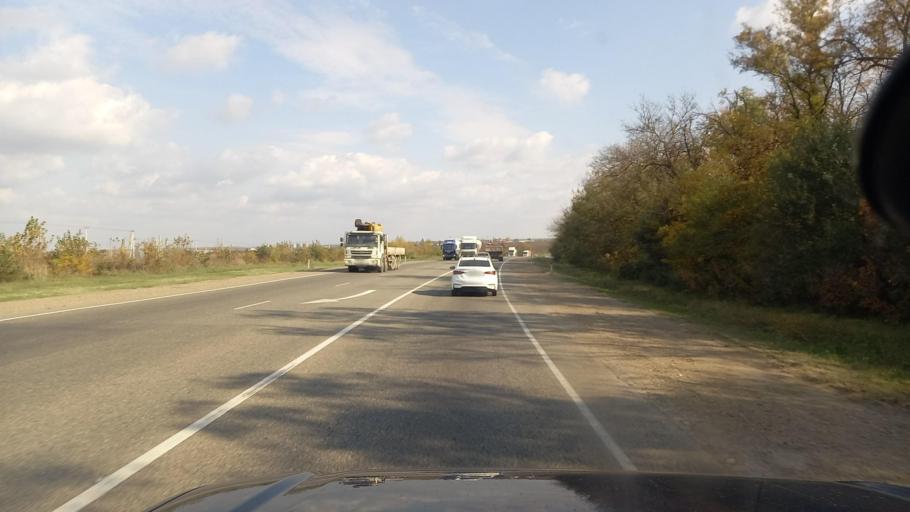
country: RU
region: Krasnodarskiy
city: Akhtyrskiy
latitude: 44.8509
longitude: 38.3174
